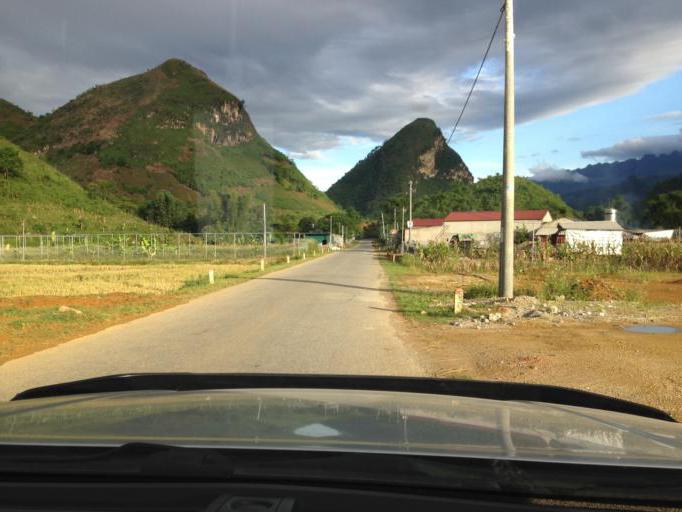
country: VN
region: Lai Chau
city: Lai Chau
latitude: 22.3522
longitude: 103.5050
